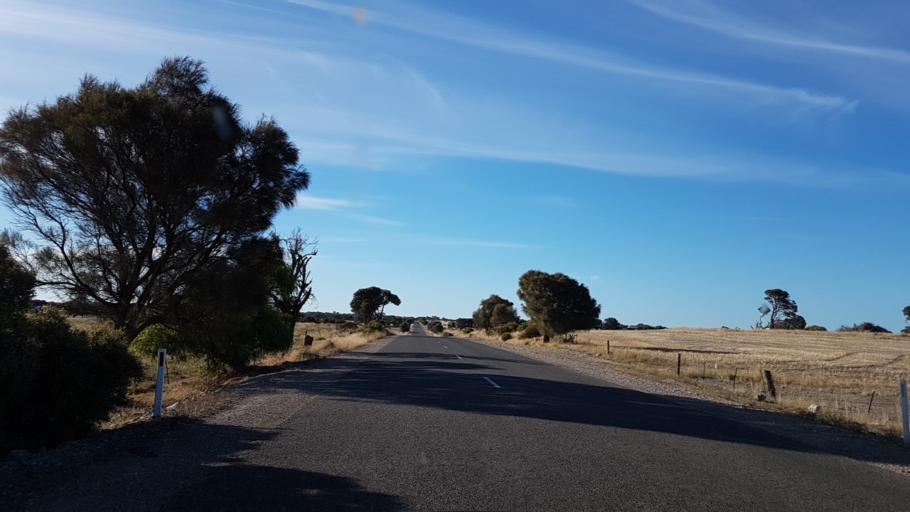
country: AU
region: South Australia
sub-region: Yorke Peninsula
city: Honiton
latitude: -34.9447
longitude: 137.0954
